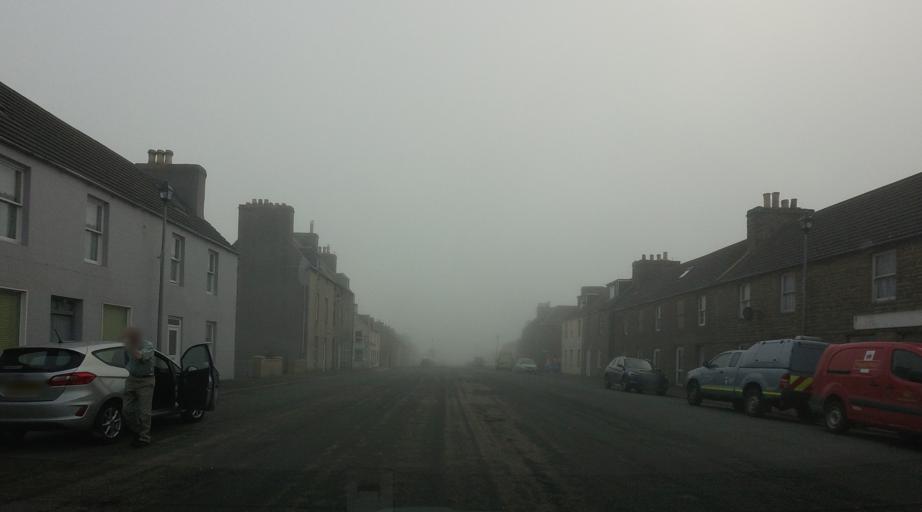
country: GB
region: Scotland
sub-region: Highland
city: Wick
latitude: 58.3019
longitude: -3.2847
